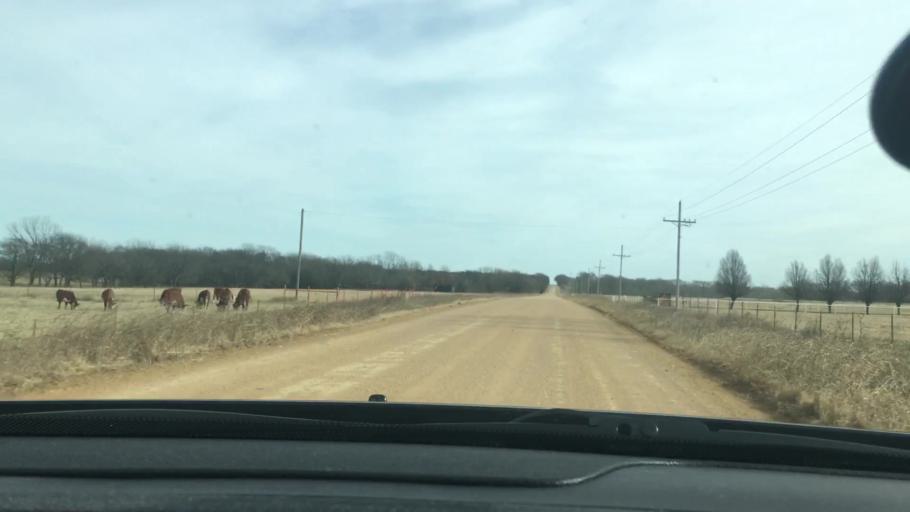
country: US
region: Oklahoma
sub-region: Murray County
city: Sulphur
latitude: 34.4050
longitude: -96.9117
